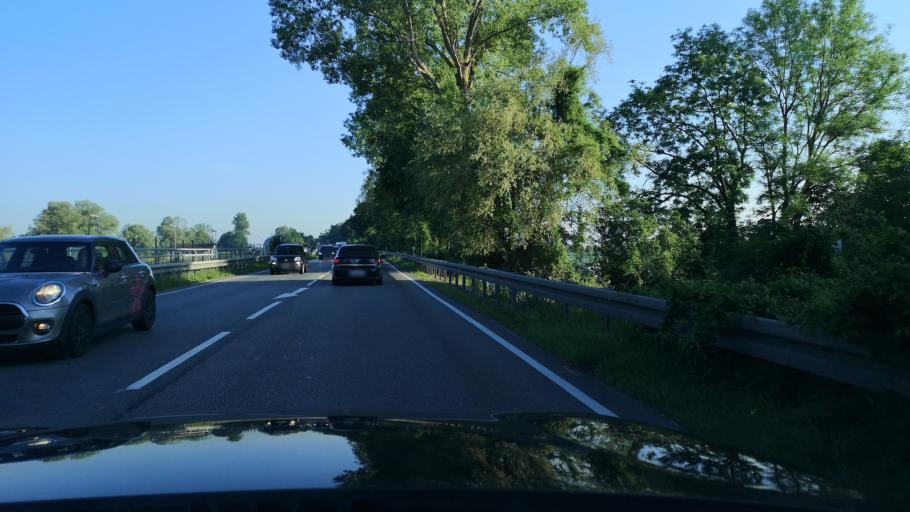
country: DE
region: Bavaria
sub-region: Upper Bavaria
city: Ismaning
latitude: 48.2040
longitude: 11.7010
